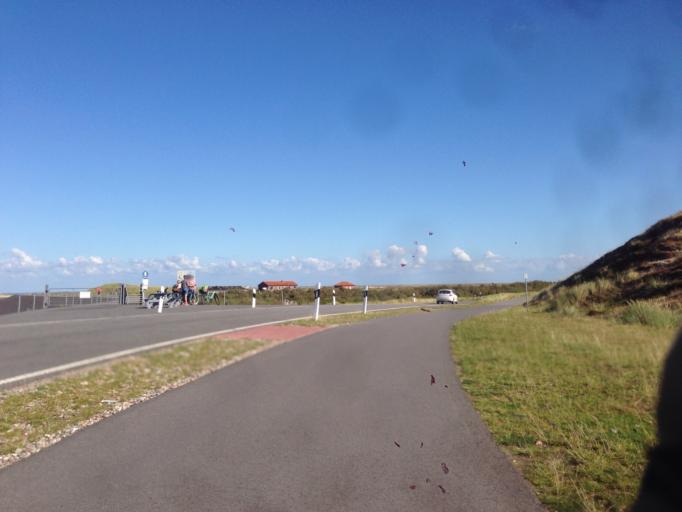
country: DE
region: Schleswig-Holstein
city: List
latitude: 55.0337
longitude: 8.4102
